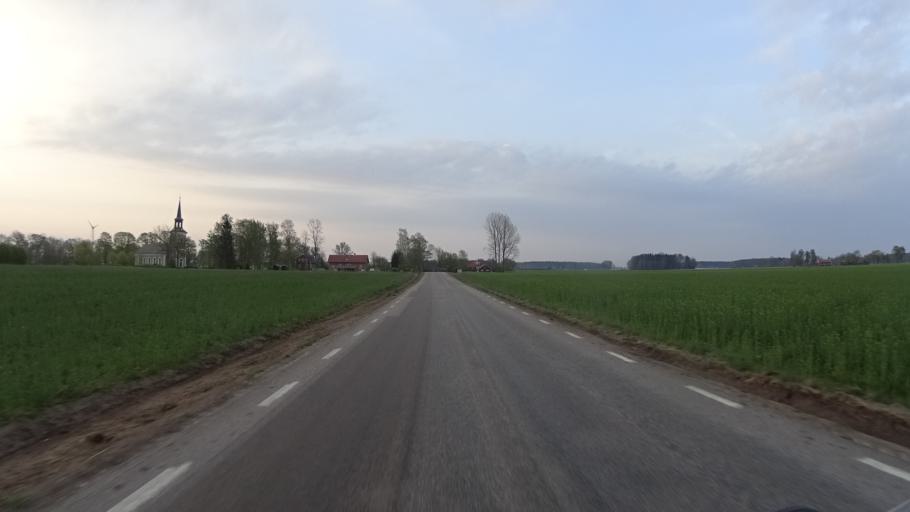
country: SE
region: Vaestra Goetaland
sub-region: Gotene Kommun
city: Kallby
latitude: 58.4749
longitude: 13.3244
